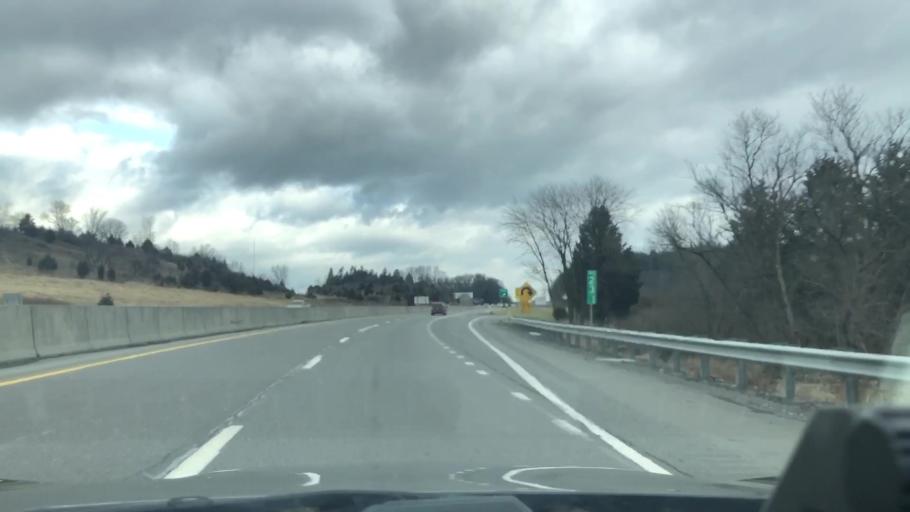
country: US
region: Pennsylvania
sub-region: Monroe County
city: Saylorsburg
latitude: 40.9271
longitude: -75.2979
